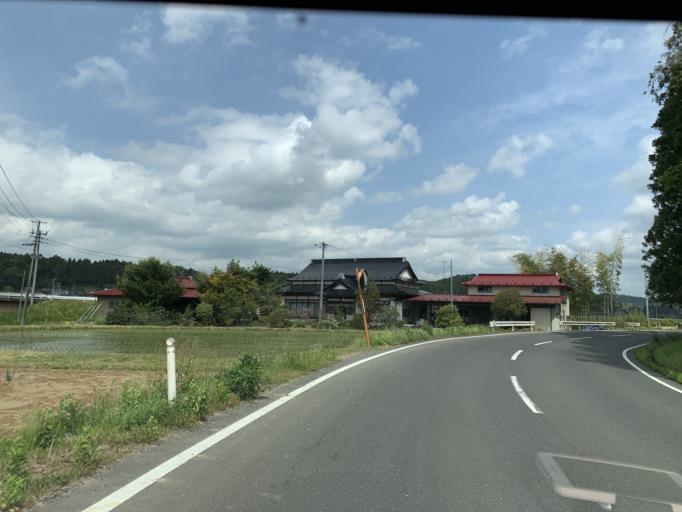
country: JP
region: Iwate
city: Ichinoseki
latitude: 38.8344
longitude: 141.0186
